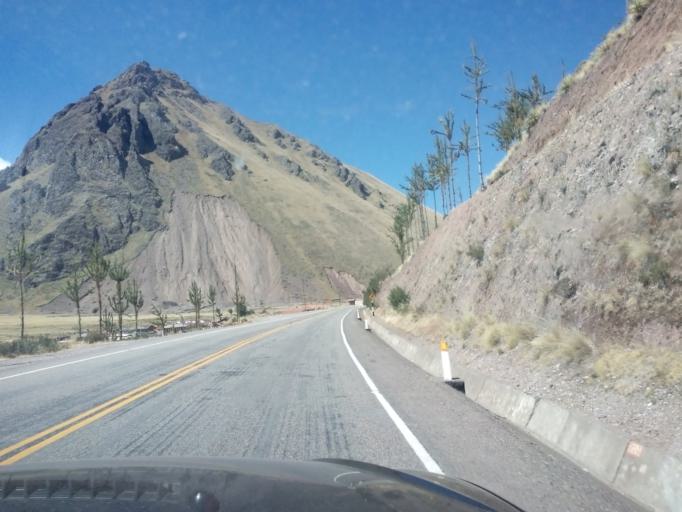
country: PE
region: Cusco
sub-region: Provincia de Canas
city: Layo
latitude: -14.4504
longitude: -71.0757
